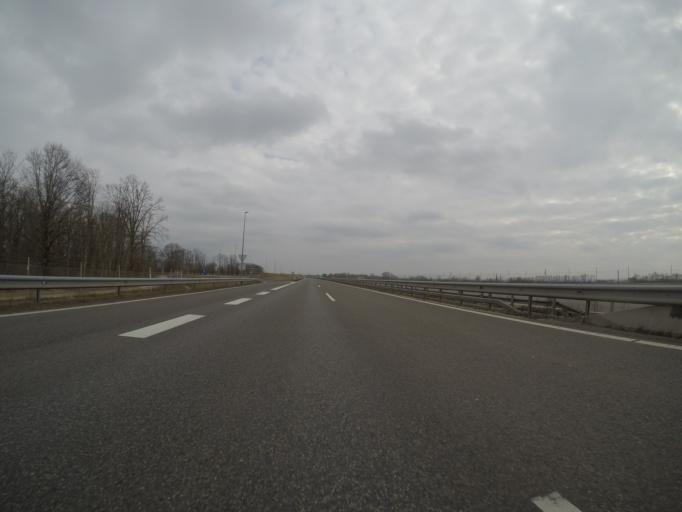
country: SI
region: Turnisce
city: Turnisce
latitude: 46.6193
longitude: 16.3017
